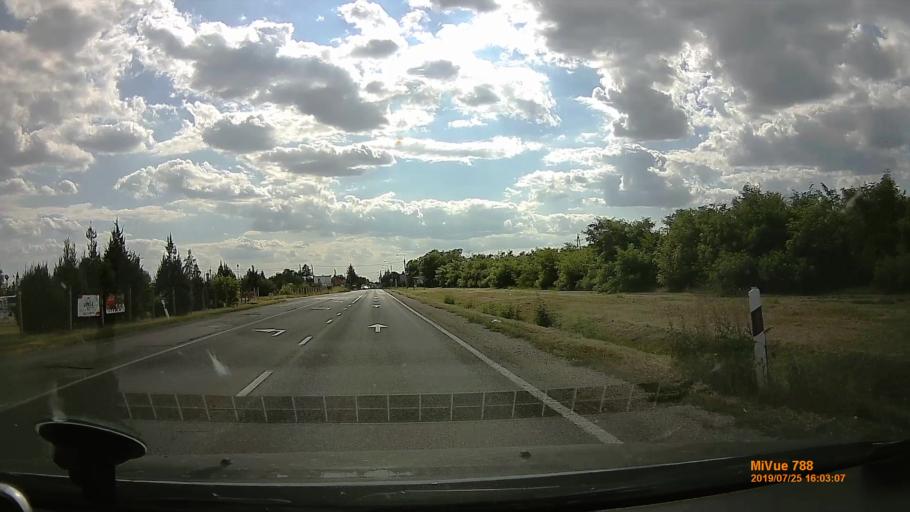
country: HU
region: Heves
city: Szihalom
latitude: 47.7813
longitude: 20.4863
